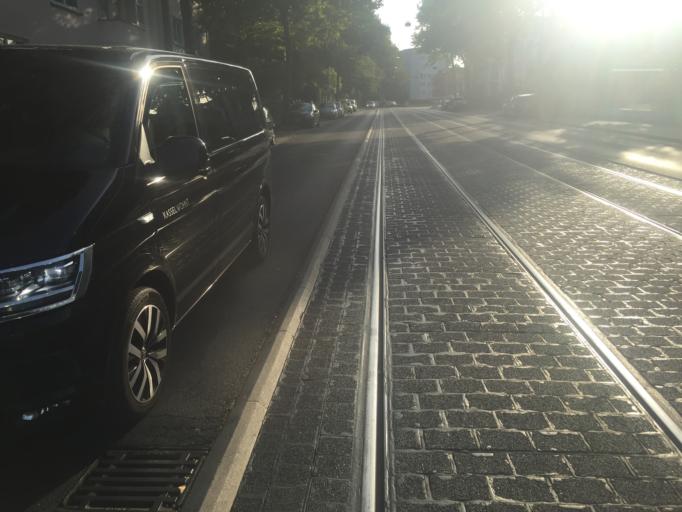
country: DE
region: Hesse
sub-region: Regierungsbezirk Kassel
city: Kassel
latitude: 51.3123
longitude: 9.4427
